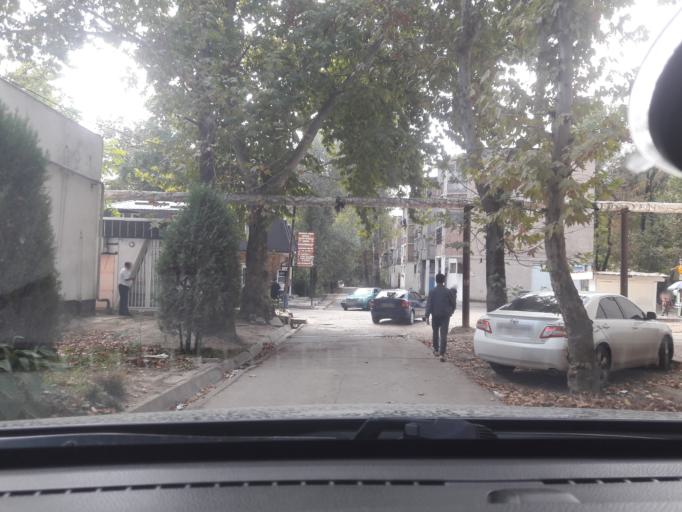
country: TJ
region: Dushanbe
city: Dushanbe
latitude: 38.5875
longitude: 68.7500
